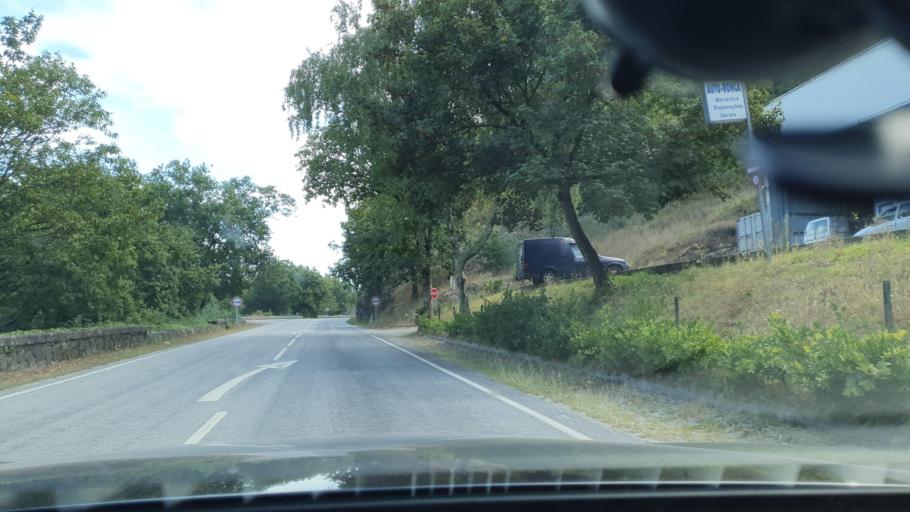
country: PT
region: Braga
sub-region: Vieira do Minho
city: Vieira do Minho
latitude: 41.6771
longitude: -8.1291
